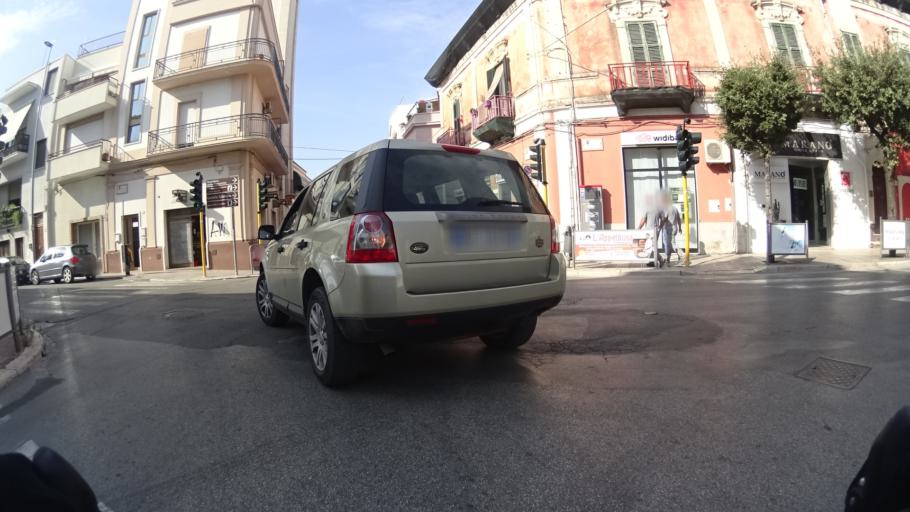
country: IT
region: Apulia
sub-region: Provincia di Taranto
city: Grottaglie
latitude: 40.5355
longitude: 17.4328
